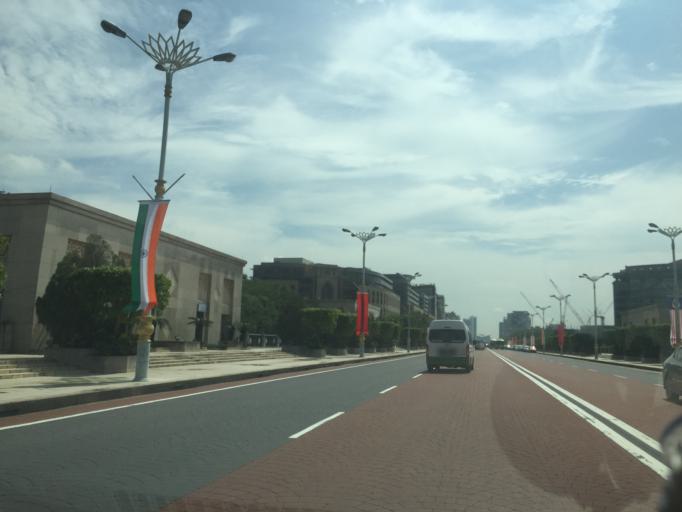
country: MY
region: Putrajaya
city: Putrajaya
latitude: 2.9326
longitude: 101.6902
